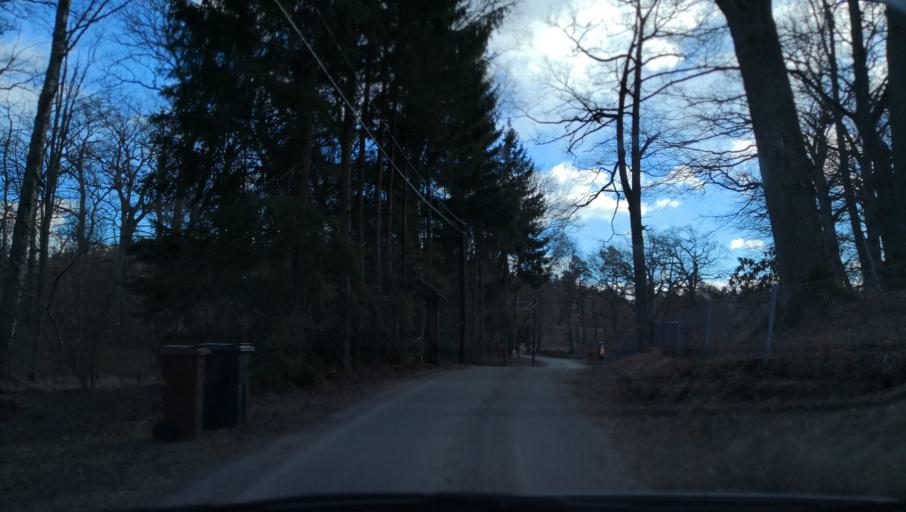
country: SE
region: Stockholm
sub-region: Varmdo Kommun
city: Mortnas
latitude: 59.3898
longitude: 18.4542
